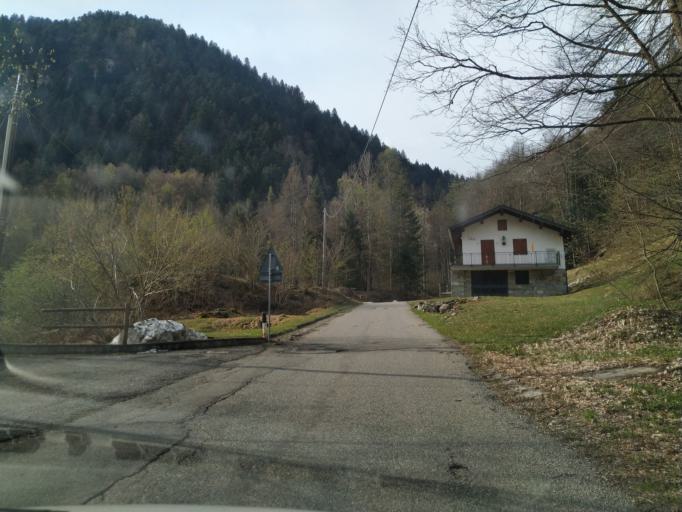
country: IT
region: Piedmont
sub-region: Provincia di Vercelli
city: Piode
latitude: 45.7686
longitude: 8.0509
